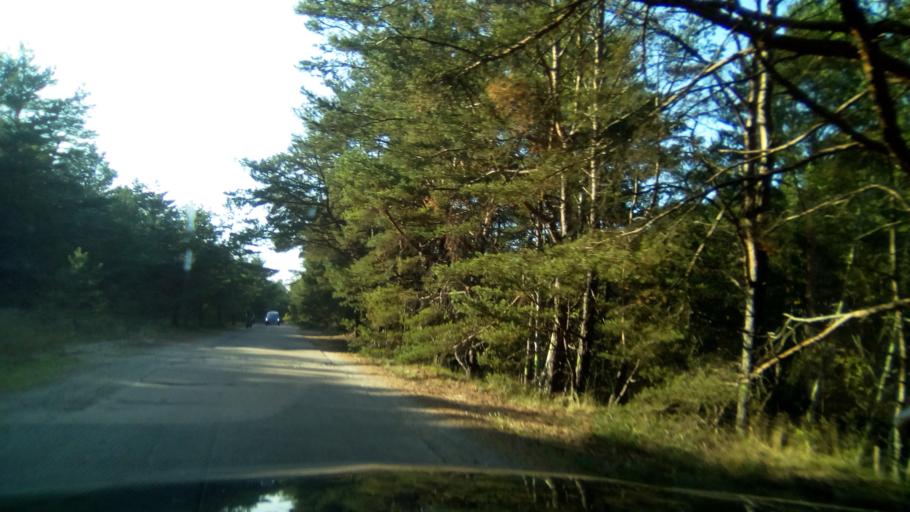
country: PL
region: West Pomeranian Voivodeship
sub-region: Swinoujscie
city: Swinoujscie
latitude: 53.9173
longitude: 14.2963
